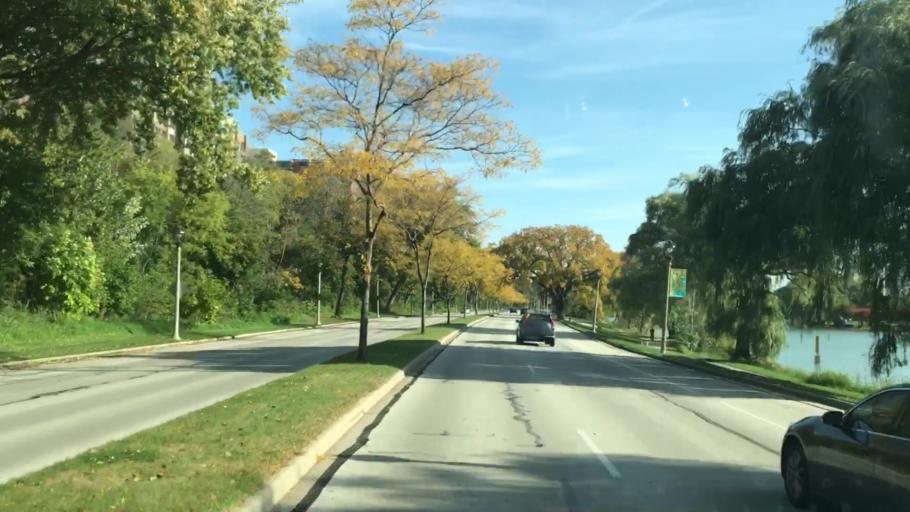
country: US
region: Wisconsin
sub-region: Milwaukee County
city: Milwaukee
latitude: 43.0471
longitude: -87.8939
